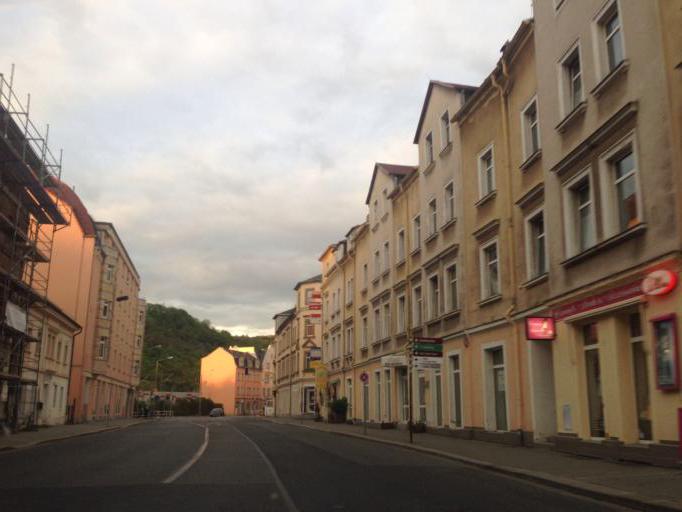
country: DE
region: Saxony
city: Freital
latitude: 51.0135
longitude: 13.6637
